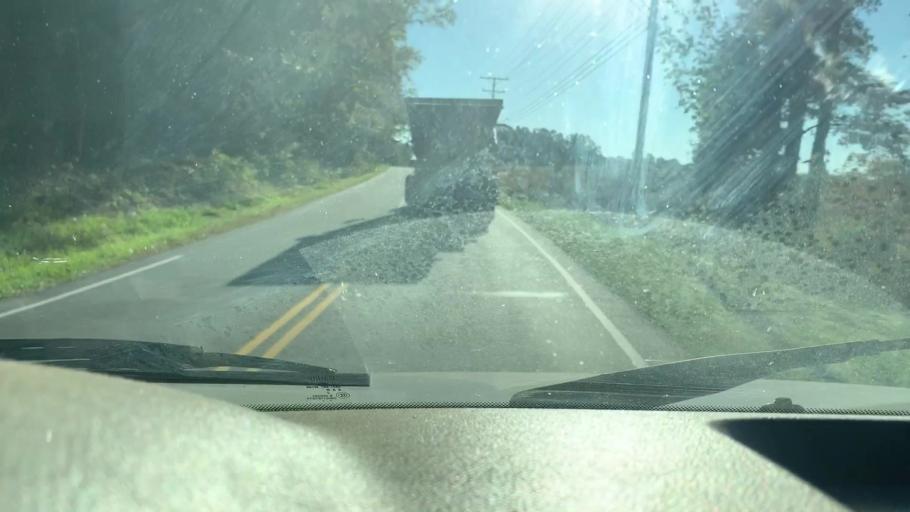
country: US
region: North Carolina
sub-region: Mecklenburg County
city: Huntersville
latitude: 35.4200
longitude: -80.7520
